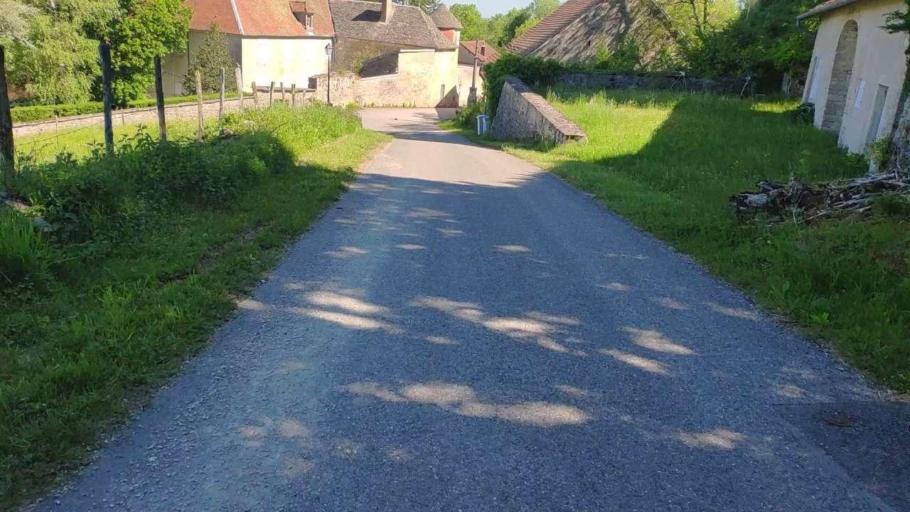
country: FR
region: Franche-Comte
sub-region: Departement du Jura
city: Clairvaux-les-Lacs
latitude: 46.6992
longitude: 5.7324
